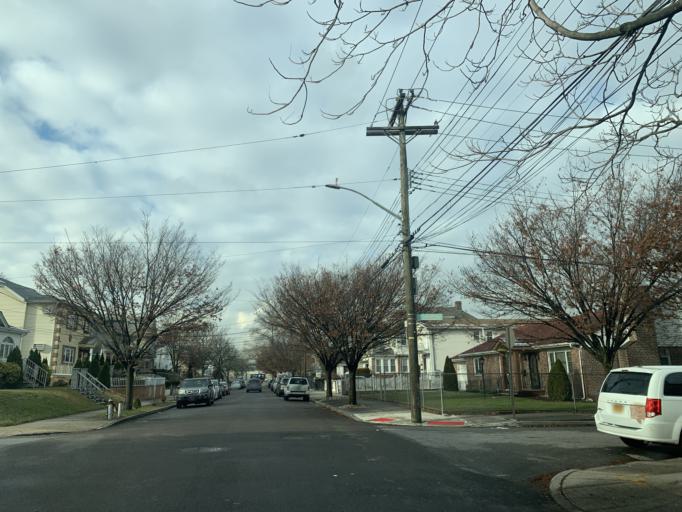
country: US
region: New York
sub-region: Queens County
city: Jamaica
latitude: 40.6862
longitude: -73.8038
